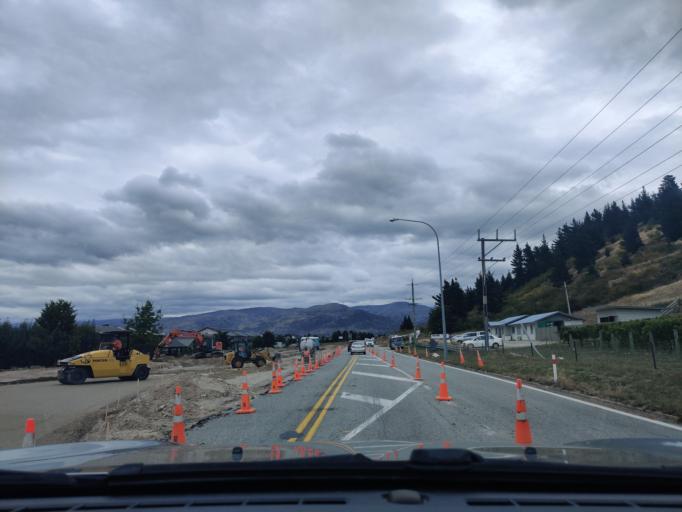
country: NZ
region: Otago
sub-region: Queenstown-Lakes District
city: Wanaka
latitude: -45.0340
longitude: 169.1920
